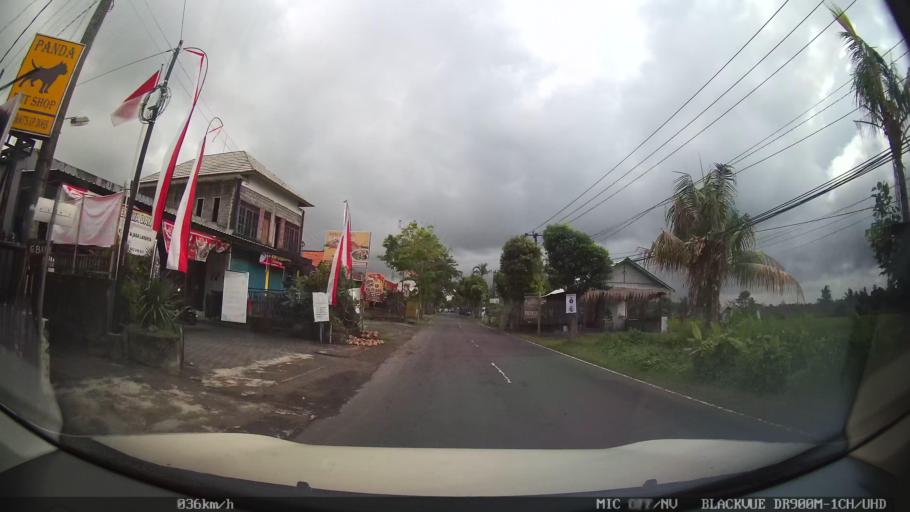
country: ID
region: Bali
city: Banjar Keraman
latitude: -8.5411
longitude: 115.2143
